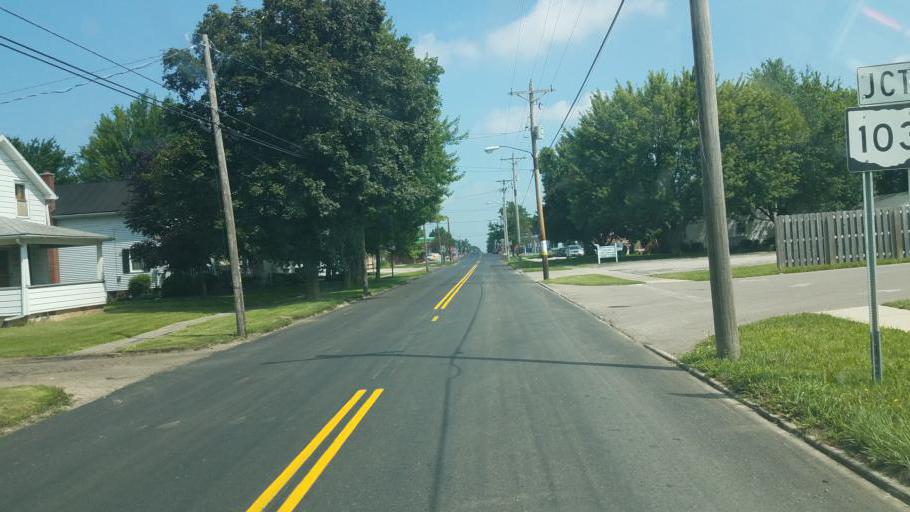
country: US
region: Ohio
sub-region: Huron County
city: Willard
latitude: 40.9598
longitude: -82.8536
